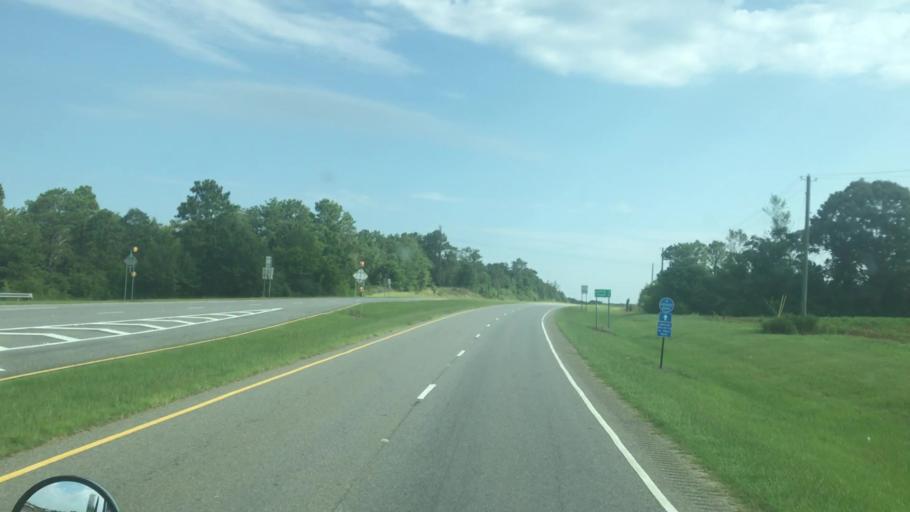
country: US
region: Georgia
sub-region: Early County
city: Blakely
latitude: 31.3920
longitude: -84.9244
